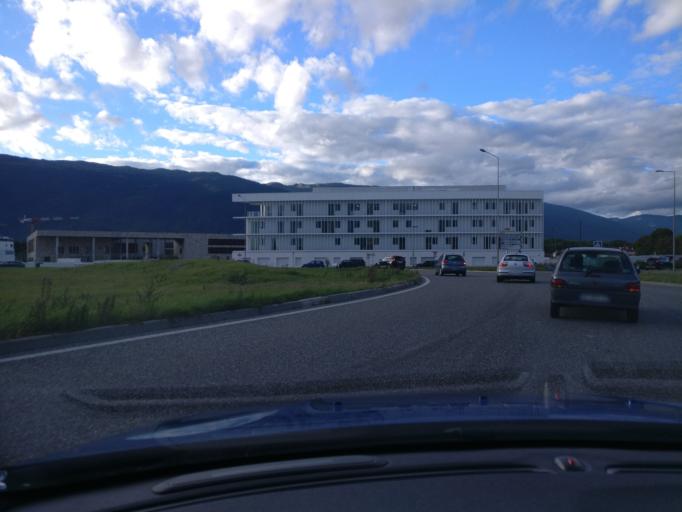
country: FR
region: Rhone-Alpes
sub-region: Departement de l'Ain
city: Saint-Genis-Pouilly
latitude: 46.2396
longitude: 6.0342
